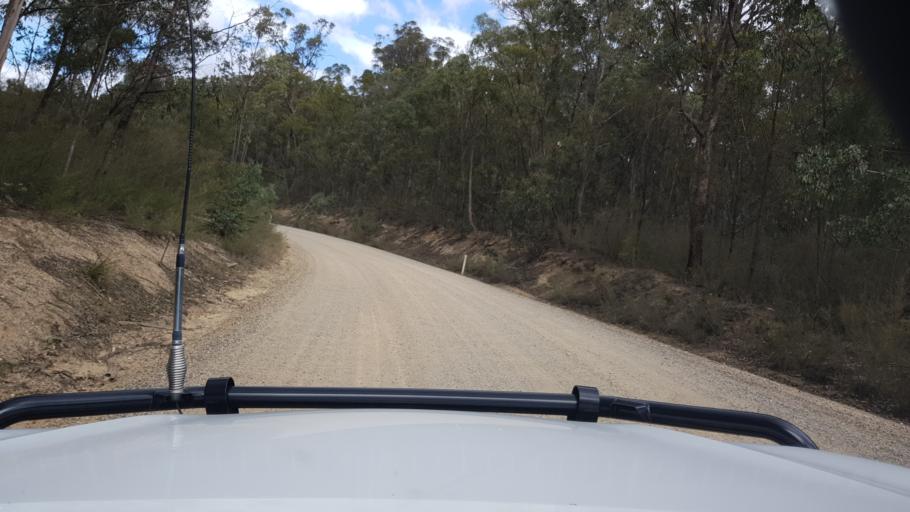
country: AU
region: Victoria
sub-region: East Gippsland
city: Bairnsdale
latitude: -37.6790
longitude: 147.5510
